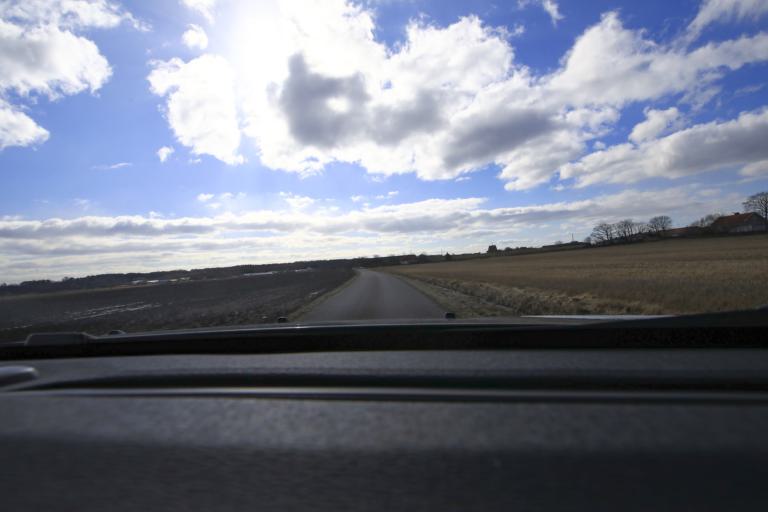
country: SE
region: Halland
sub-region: Kungsbacka Kommun
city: Frillesas
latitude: 57.2341
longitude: 12.1484
